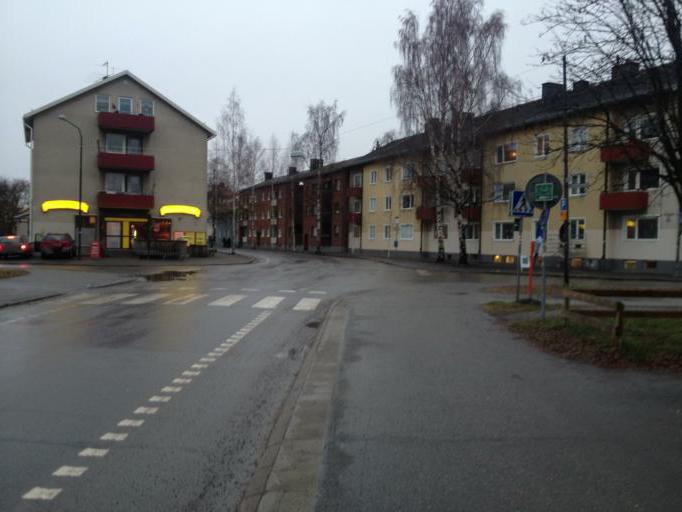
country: SE
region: Vaesterbotten
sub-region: Umea Kommun
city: Umea
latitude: 63.8219
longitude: 20.2849
